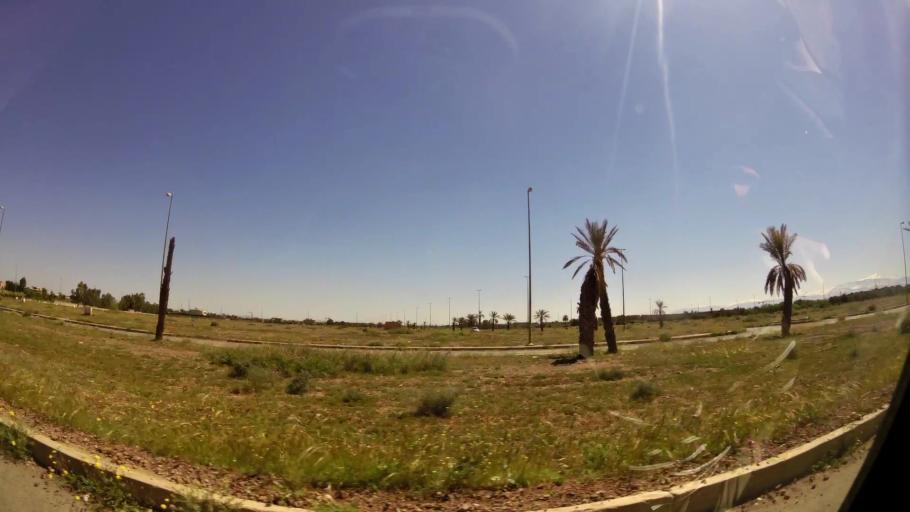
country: MA
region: Marrakech-Tensift-Al Haouz
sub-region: Marrakech
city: Marrakesh
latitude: 31.5846
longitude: -8.0051
